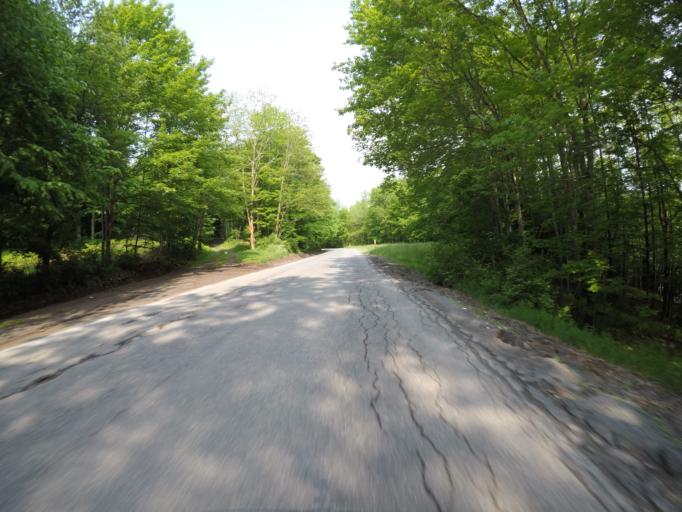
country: US
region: New York
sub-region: Sullivan County
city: Livingston Manor
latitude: 42.1119
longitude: -74.7489
